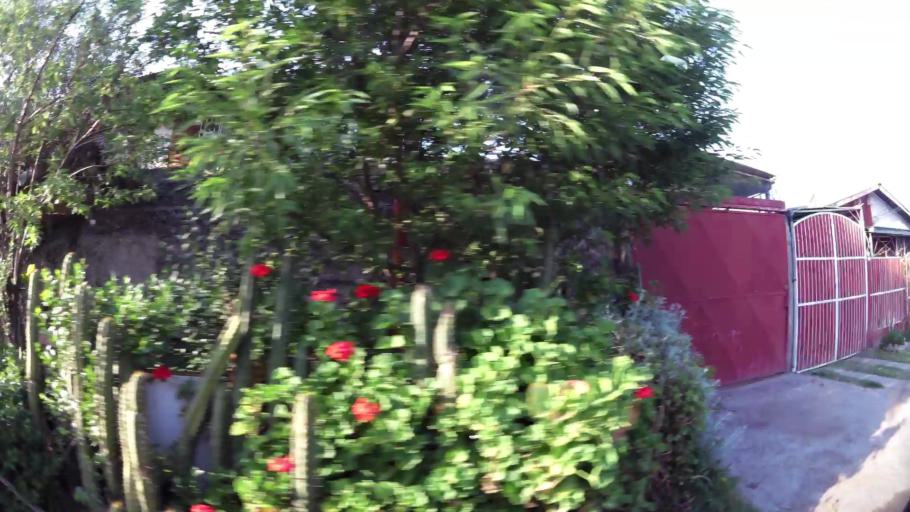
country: CL
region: Santiago Metropolitan
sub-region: Provincia de Santiago
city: Villa Presidente Frei, Nunoa, Santiago, Chile
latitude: -33.5189
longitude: -70.5836
